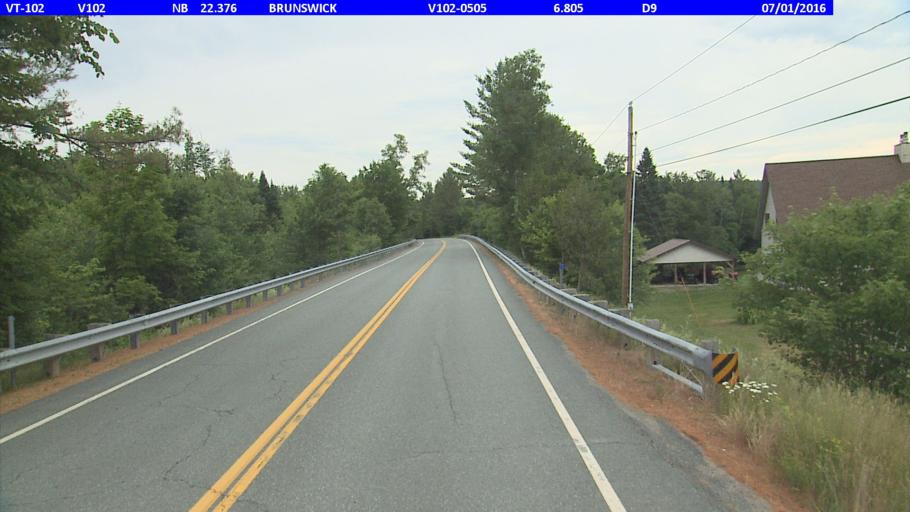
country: US
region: New Hampshire
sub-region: Coos County
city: Stratford
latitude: 44.7453
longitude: -71.6313
